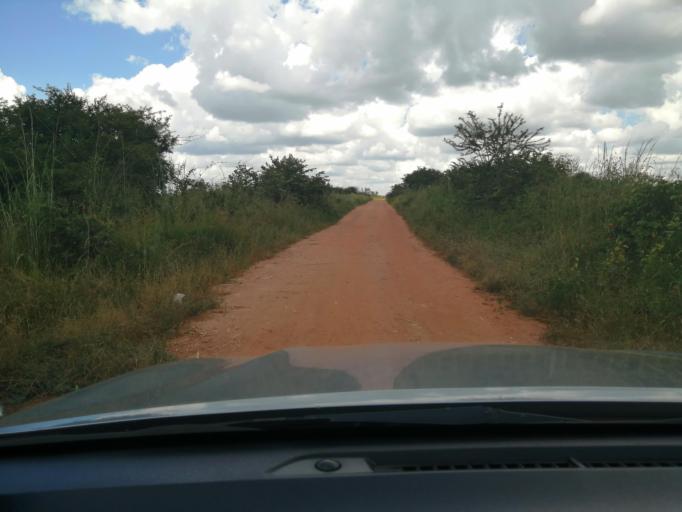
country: ZM
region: Lusaka
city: Lusaka
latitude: -15.1922
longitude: 27.9635
